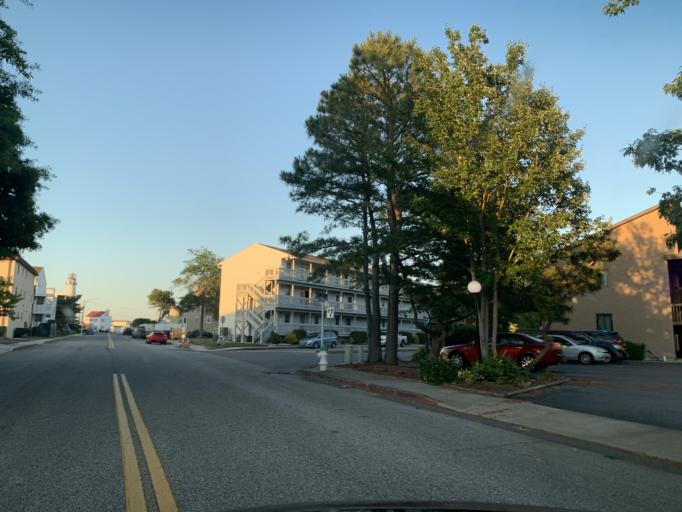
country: US
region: Delaware
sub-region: Sussex County
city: Bethany Beach
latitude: 38.4497
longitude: -75.0572
